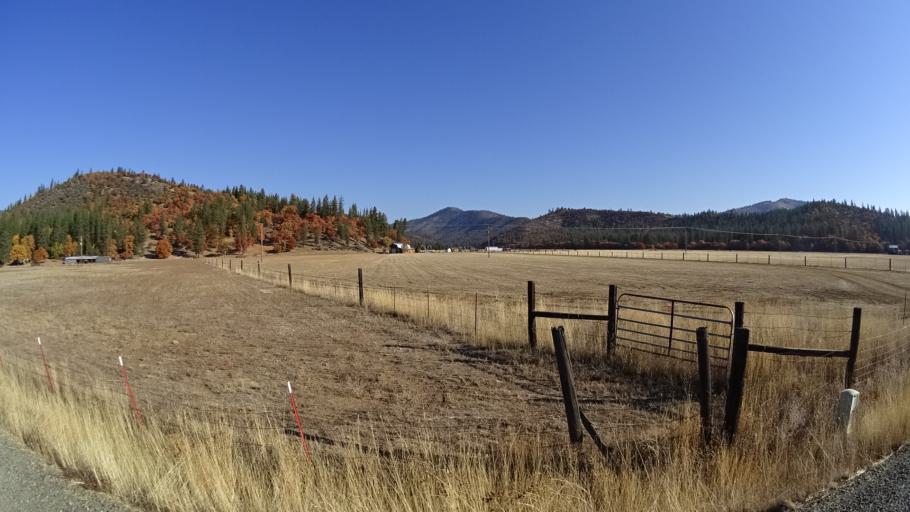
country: US
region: California
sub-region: Siskiyou County
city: Yreka
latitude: 41.6322
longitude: -122.8974
